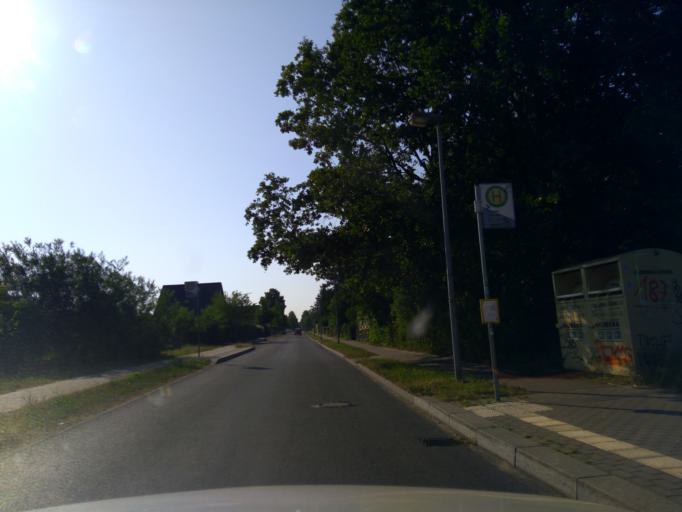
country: DE
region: Brandenburg
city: Dallgow-Doeberitz
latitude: 52.5606
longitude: 13.0666
